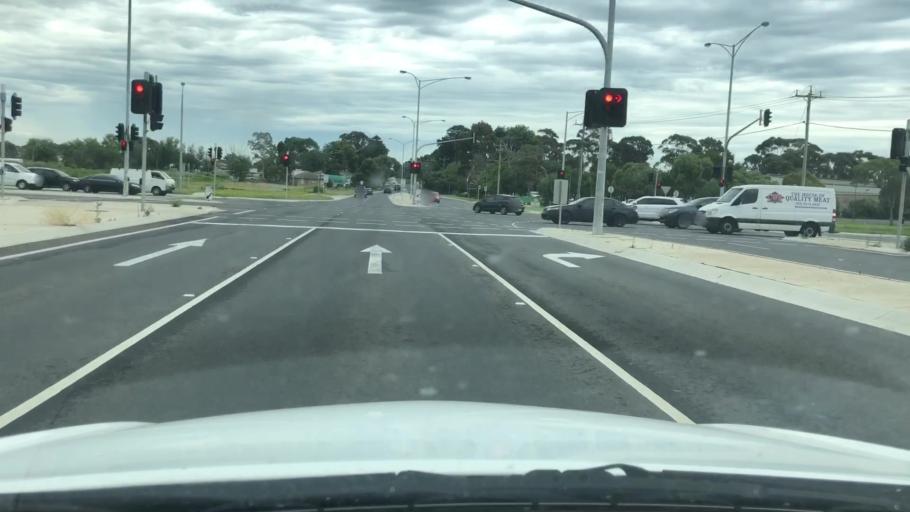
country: AU
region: Victoria
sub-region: Greater Dandenong
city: Springvale South
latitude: -37.9620
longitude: 145.1294
